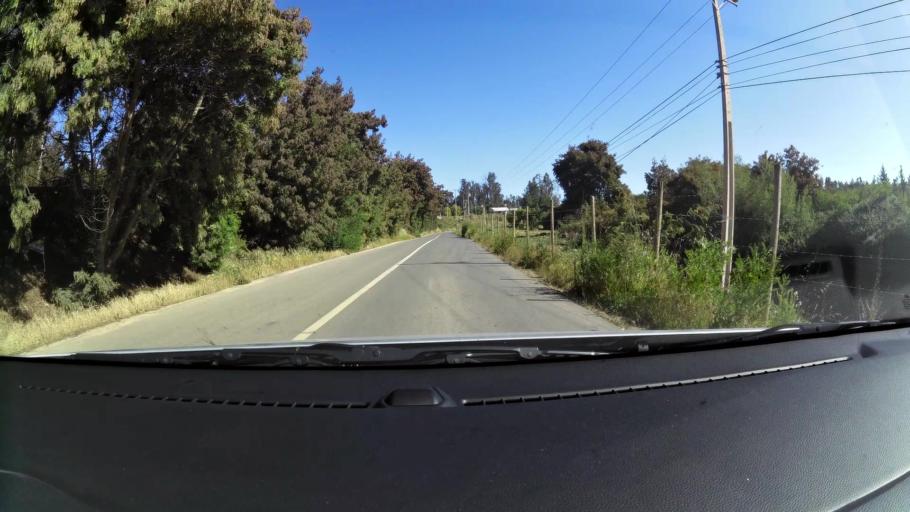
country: CL
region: Valparaiso
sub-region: Provincia de Valparaiso
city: Vina del Mar
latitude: -33.1447
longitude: -71.5611
